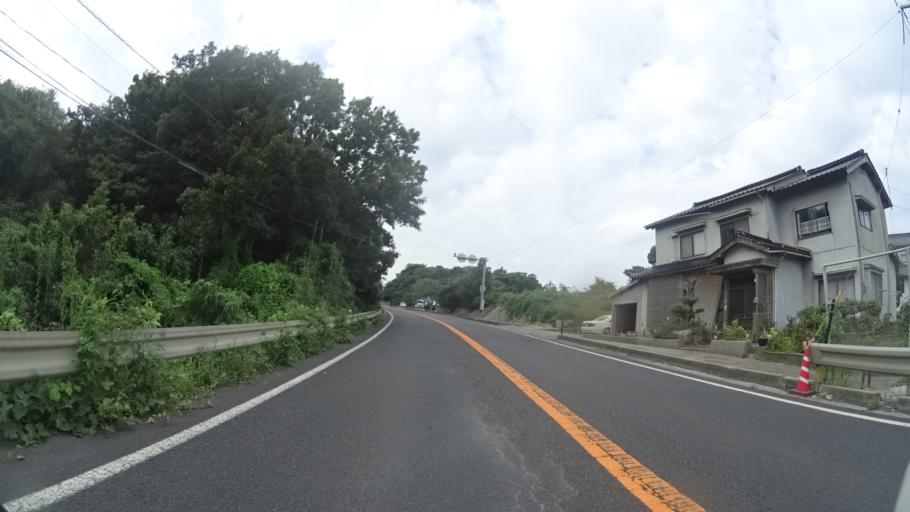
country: JP
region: Shimane
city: Odacho-oda
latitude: 35.1869
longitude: 132.4272
